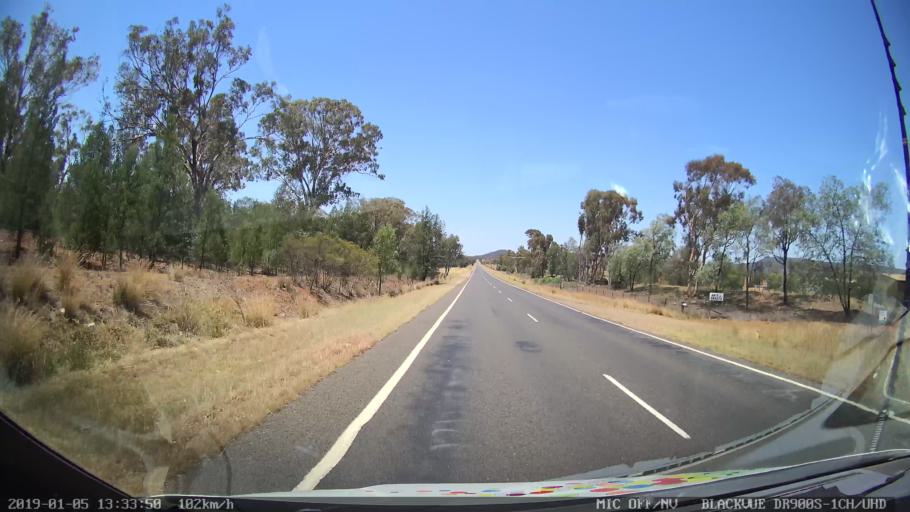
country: AU
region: New South Wales
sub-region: Gunnedah
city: Gunnedah
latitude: -30.9987
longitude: 150.1231
